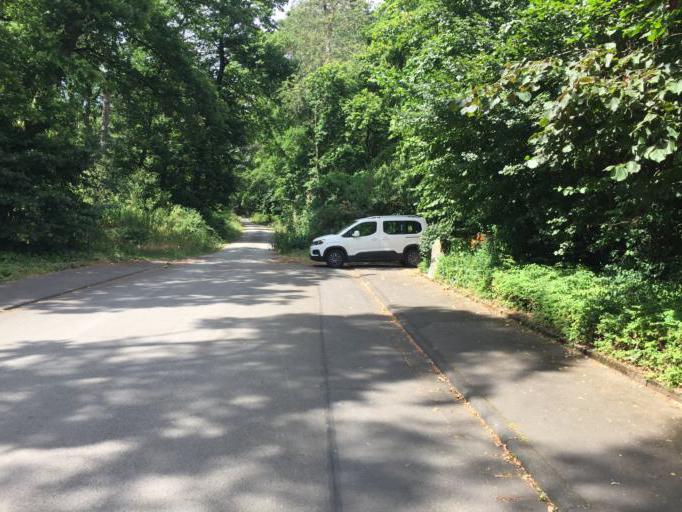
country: DE
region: Hesse
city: Lollar
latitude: 50.6486
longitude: 8.6727
